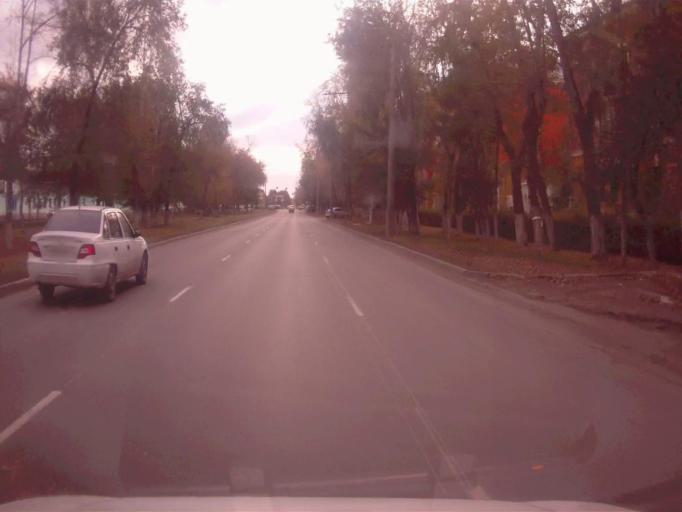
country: RU
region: Chelyabinsk
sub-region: Gorod Chelyabinsk
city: Chelyabinsk
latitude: 55.1203
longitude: 61.4721
